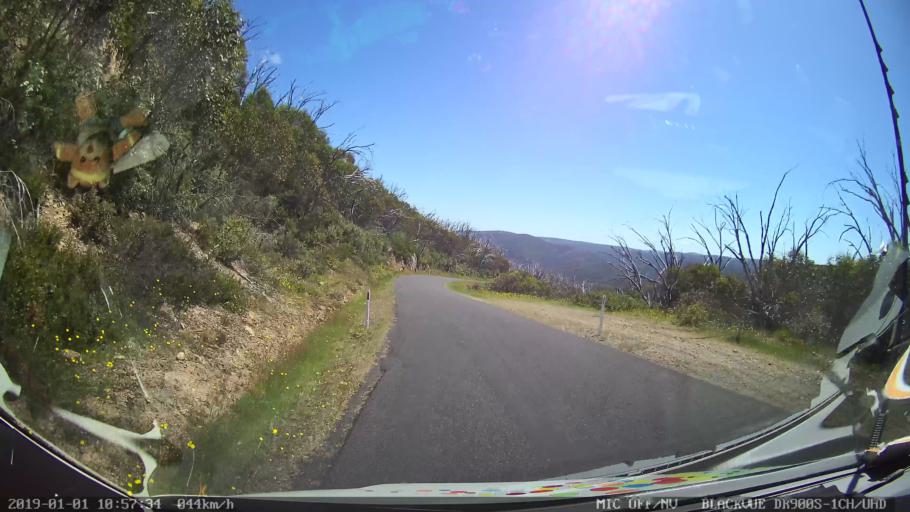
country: AU
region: New South Wales
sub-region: Snowy River
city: Jindabyne
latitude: -35.9970
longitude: 148.3967
